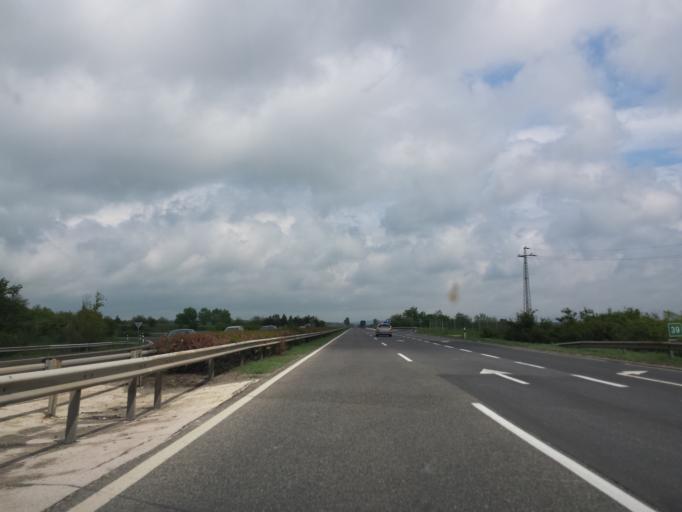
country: HU
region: Fejer
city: Bicske
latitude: 47.5001
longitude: 18.5942
